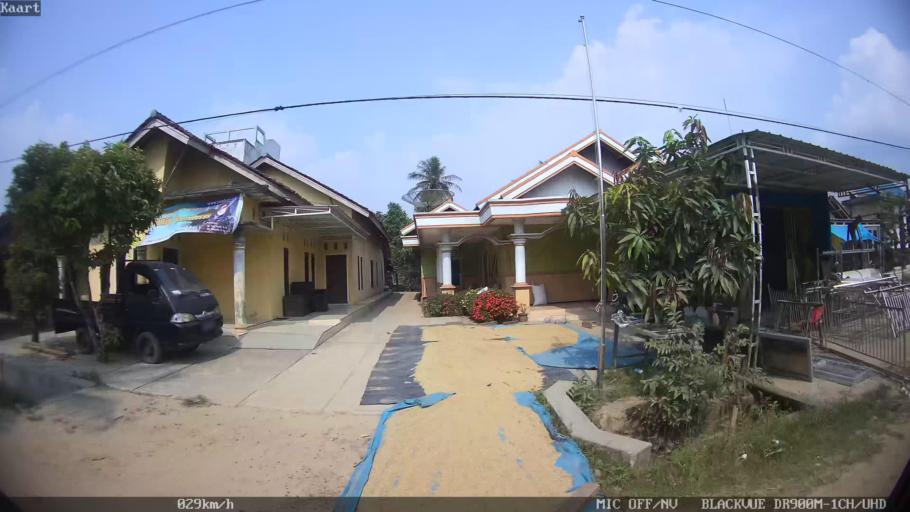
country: ID
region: Lampung
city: Pringsewu
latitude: -5.3993
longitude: 104.9930
